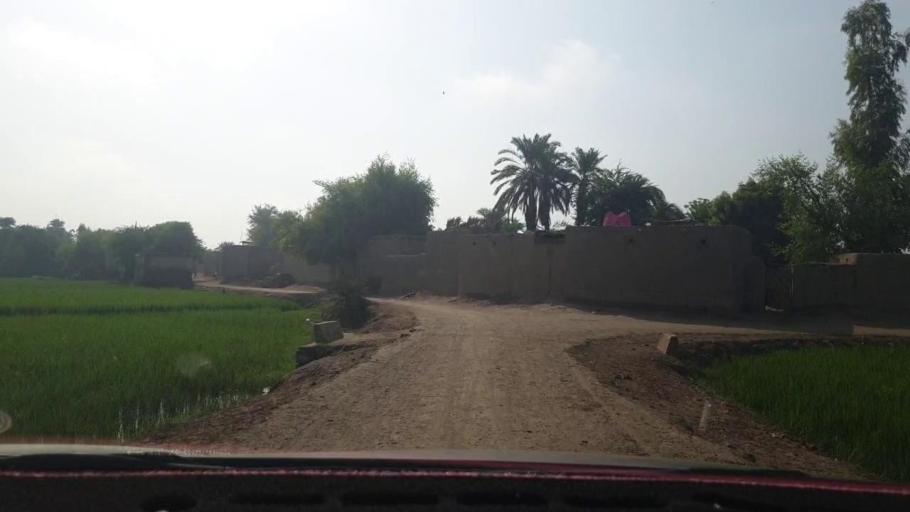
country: PK
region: Sindh
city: Nasirabad
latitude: 27.4545
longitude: 67.9615
